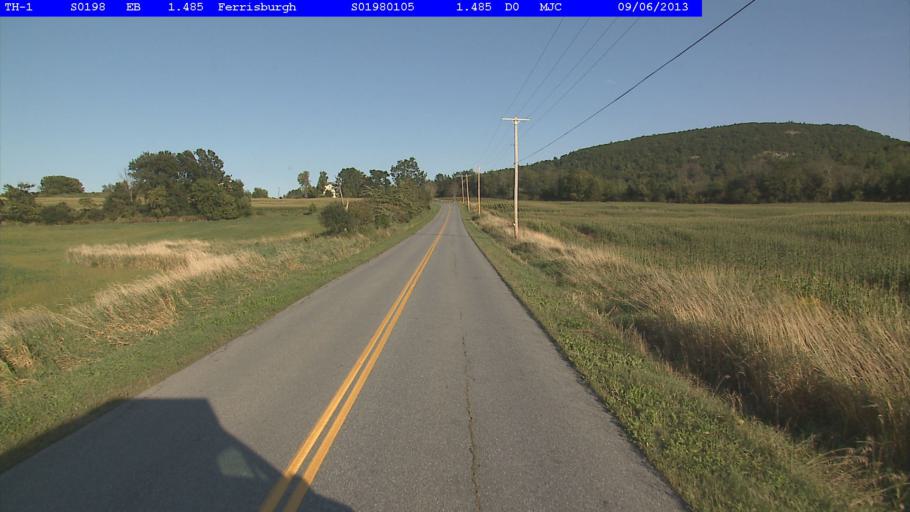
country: US
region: Vermont
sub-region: Addison County
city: Vergennes
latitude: 44.2557
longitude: -73.1994
